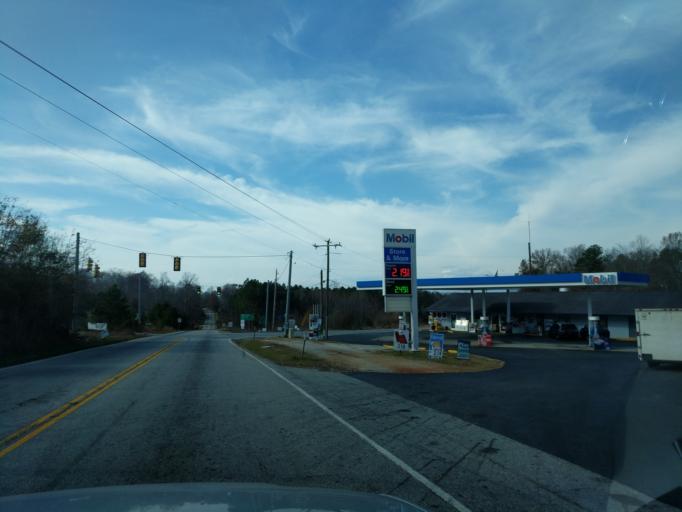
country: US
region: South Carolina
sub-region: Pickens County
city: Pickens
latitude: 34.8786
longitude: -82.7246
